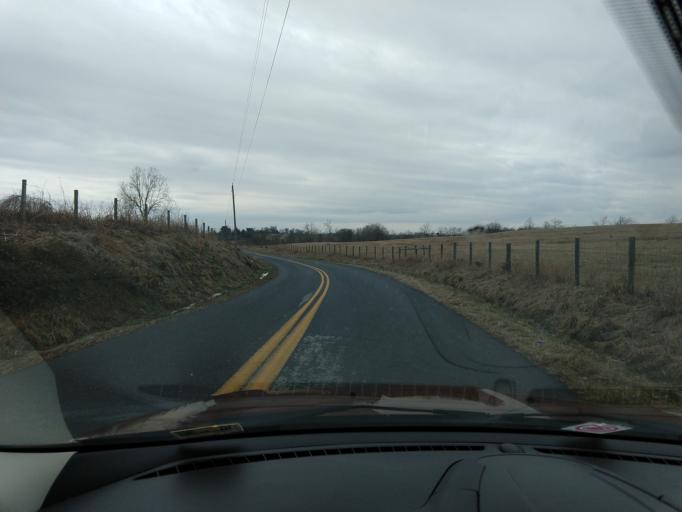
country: US
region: Virginia
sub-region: Augusta County
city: Weyers Cave
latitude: 38.2267
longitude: -78.8847
